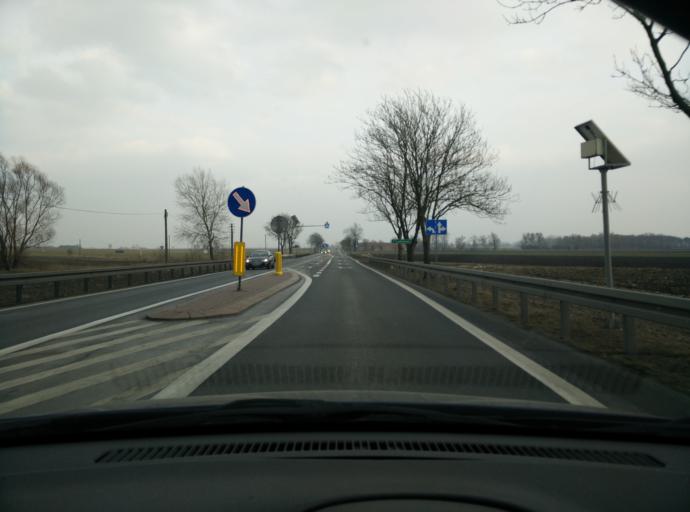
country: PL
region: Greater Poland Voivodeship
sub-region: Powiat poznanski
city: Kornik
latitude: 52.2436
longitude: 17.1307
